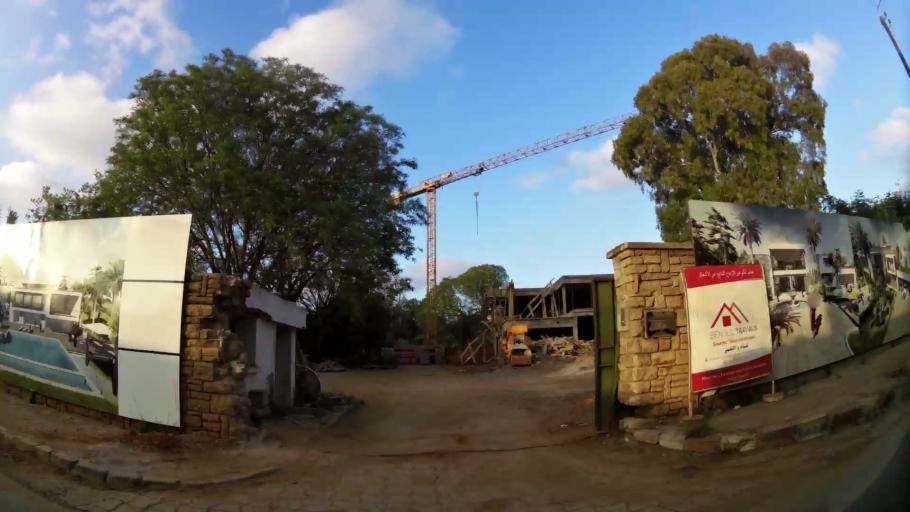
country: MA
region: Rabat-Sale-Zemmour-Zaer
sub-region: Rabat
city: Rabat
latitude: 33.9797
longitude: -6.8322
